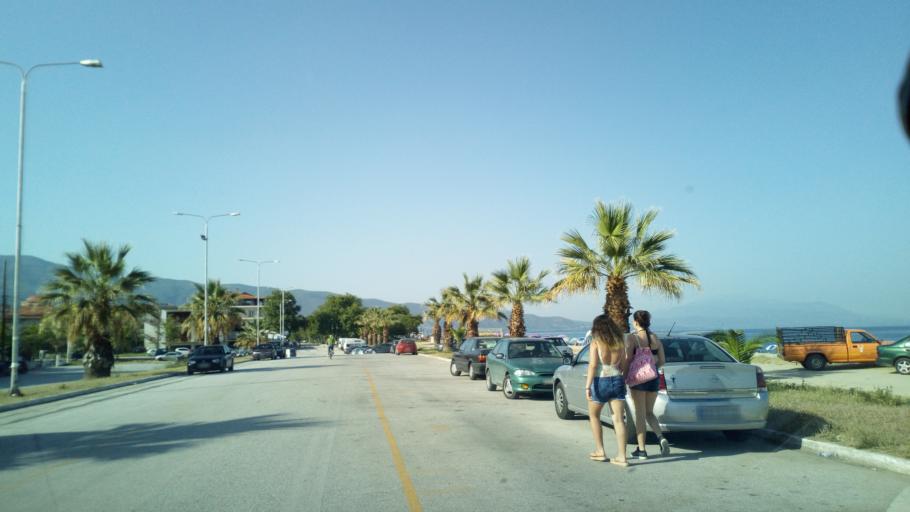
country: GR
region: Central Macedonia
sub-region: Nomos Thessalonikis
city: Nea Vrasna
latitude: 40.7153
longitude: 23.7068
